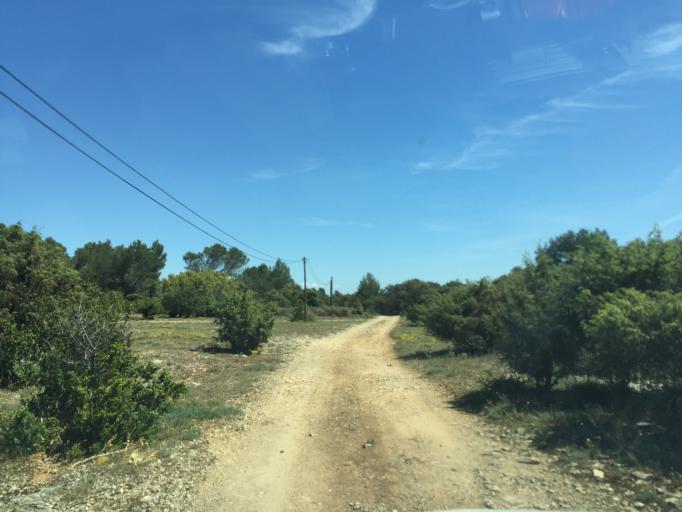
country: FR
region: Provence-Alpes-Cote d'Azur
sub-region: Departement du Vaucluse
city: Chateauneuf-du-Pape
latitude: 44.0524
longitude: 4.8053
